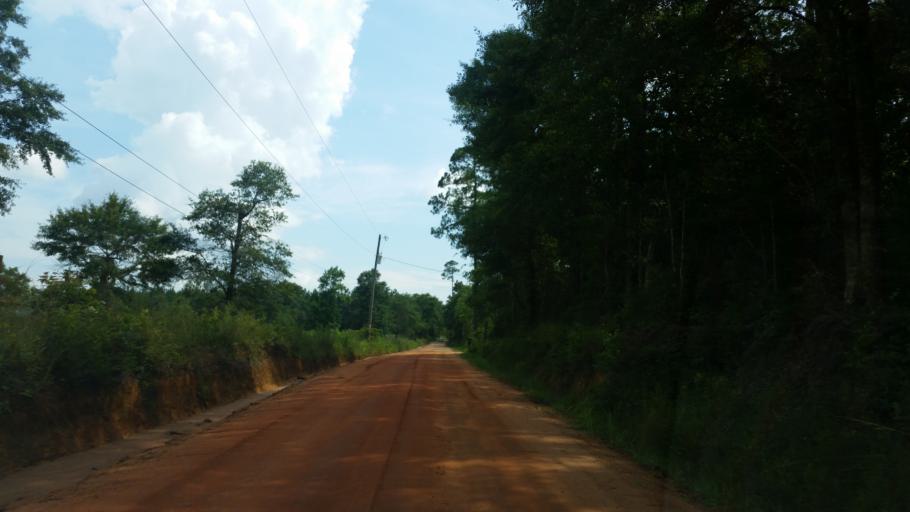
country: US
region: Florida
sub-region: Escambia County
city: Cantonment
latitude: 30.6253
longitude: -87.3836
